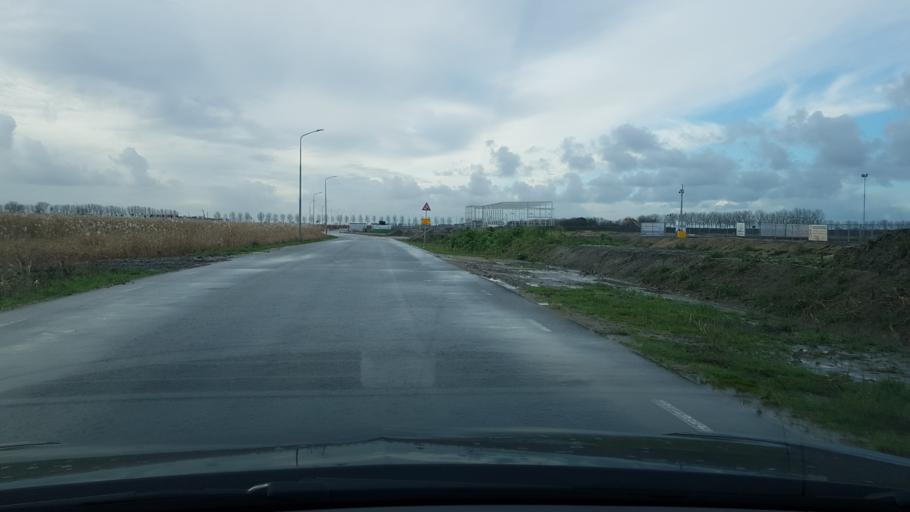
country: NL
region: North Holland
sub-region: Gemeente Haarlemmermeer
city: Hoofddorp
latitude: 52.2793
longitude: 4.7019
